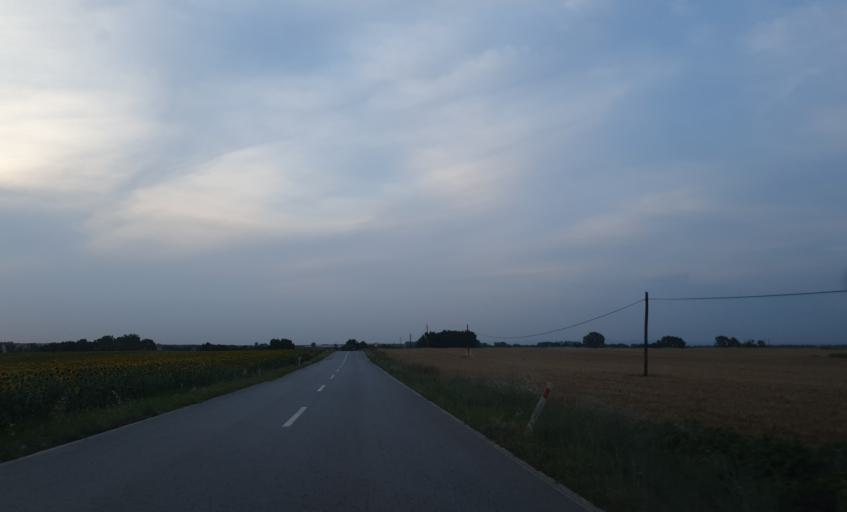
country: TR
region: Kirklareli
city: Buyukkaristiran
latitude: 41.3557
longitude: 27.6070
